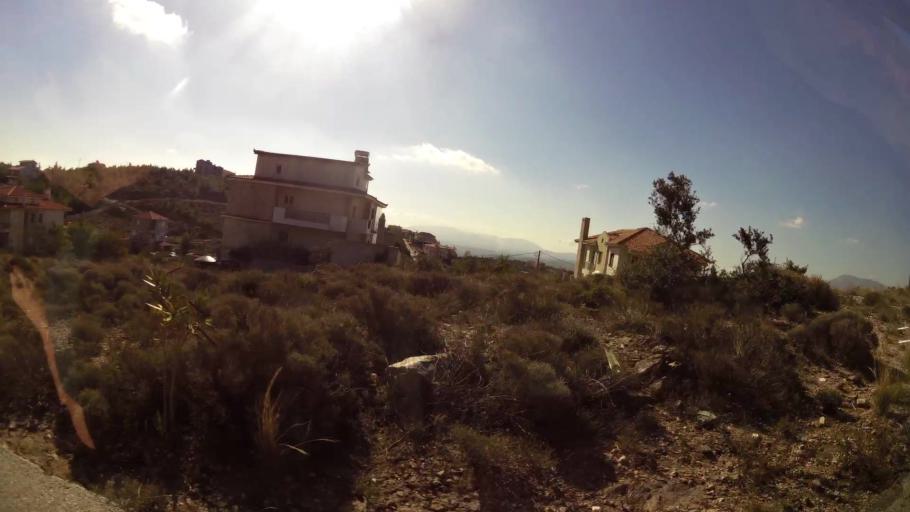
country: GR
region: Attica
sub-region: Nomarchia Anatolikis Attikis
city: Dioni
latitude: 38.0380
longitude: 23.9295
